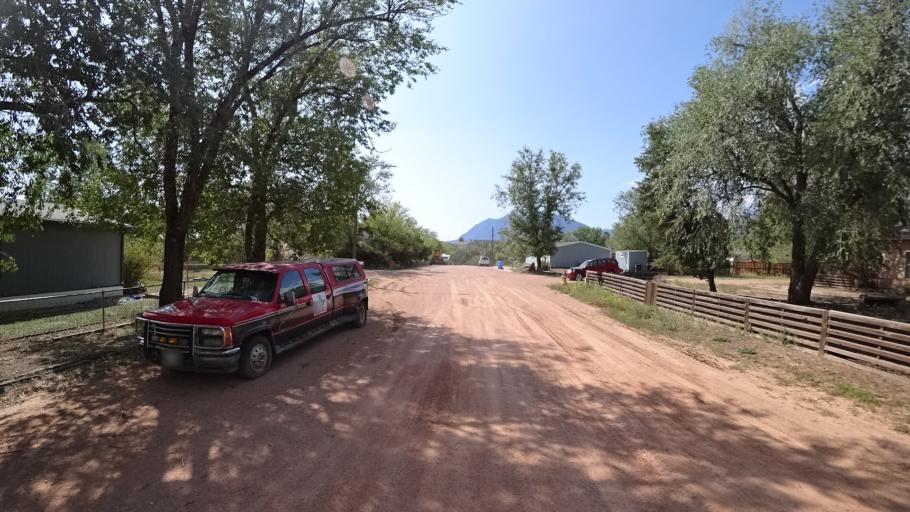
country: US
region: Colorado
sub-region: El Paso County
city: Colorado Springs
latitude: 38.8295
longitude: -104.8466
